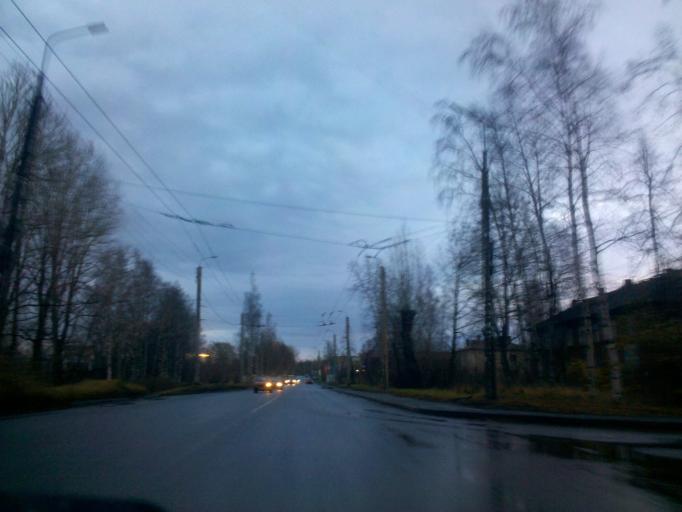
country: RU
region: Republic of Karelia
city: Petrozavodsk
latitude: 61.7785
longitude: 34.4080
